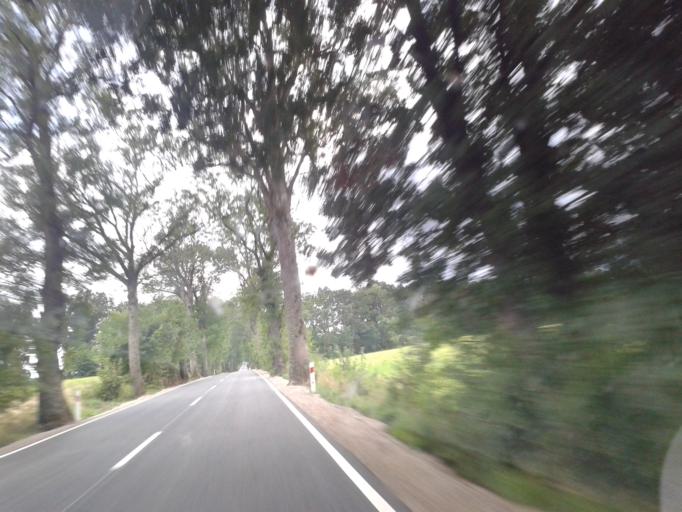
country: PL
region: West Pomeranian Voivodeship
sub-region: Powiat szczecinecki
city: Grzmiaca
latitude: 53.8621
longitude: 16.4784
